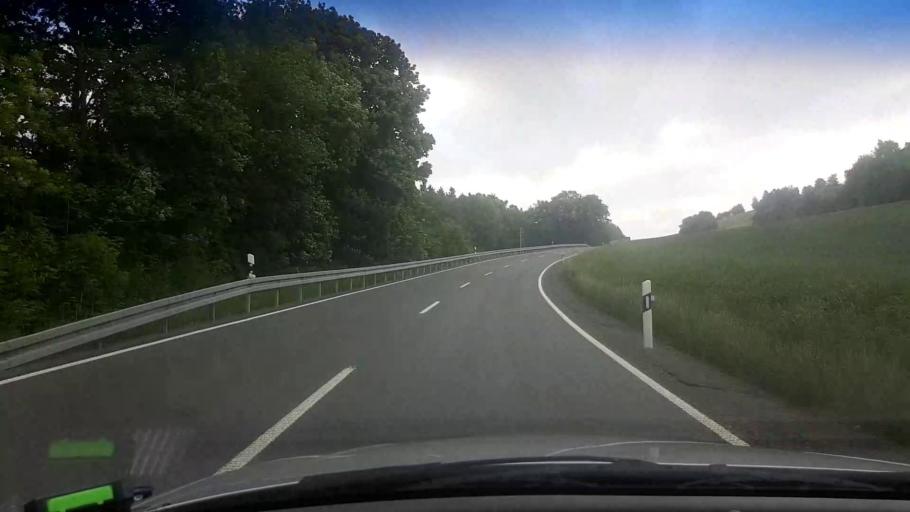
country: DE
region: Bavaria
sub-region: Upper Franconia
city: Reuth
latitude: 49.9898
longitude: 11.6869
